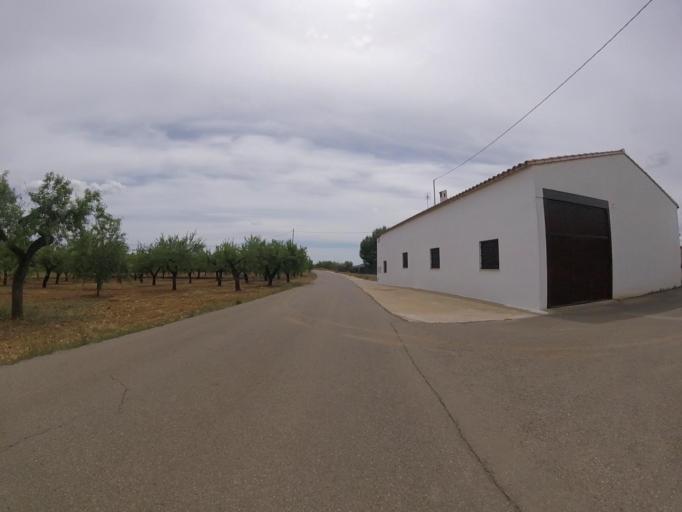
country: ES
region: Valencia
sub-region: Provincia de Castello
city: Benlloch
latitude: 40.1967
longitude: -0.0076
